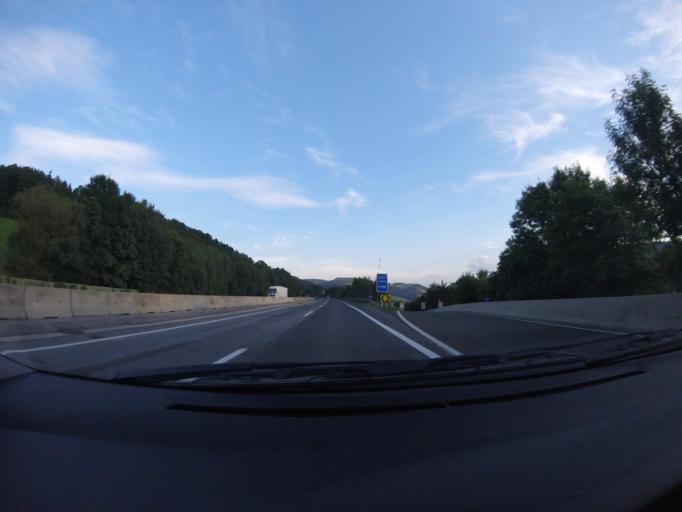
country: AT
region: Lower Austria
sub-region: Politischer Bezirk Neunkirchen
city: Grimmenstein
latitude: 47.6127
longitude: 16.1292
